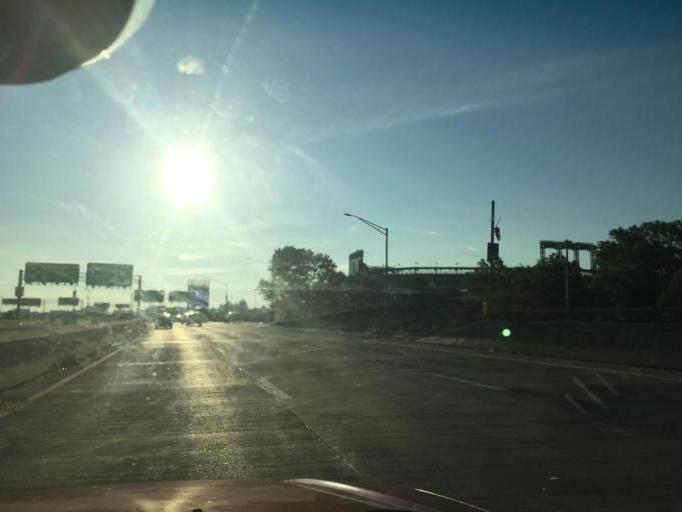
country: US
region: New York
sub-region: Queens County
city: Borough of Queens
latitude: 40.7576
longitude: -73.8516
